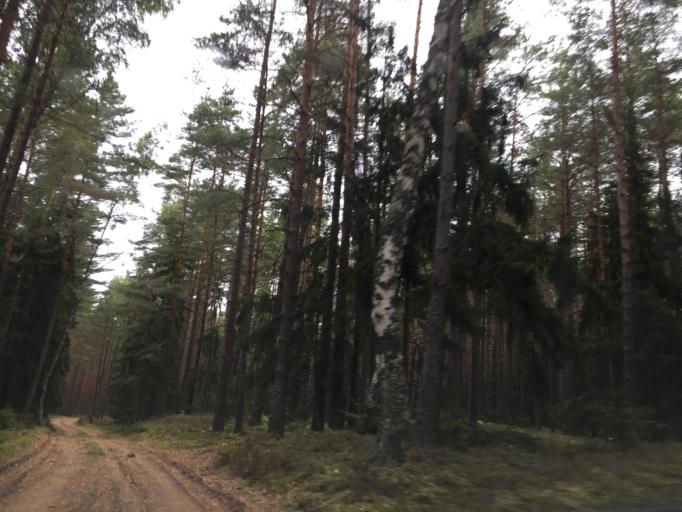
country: LV
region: Salacgrivas
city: Salacgriva
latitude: 57.7067
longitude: 24.3542
